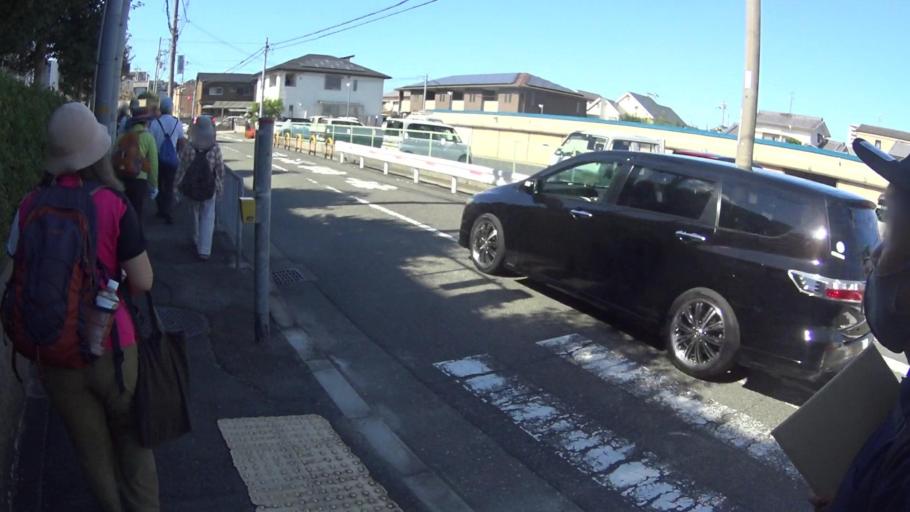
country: JP
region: Osaka
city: Izumi
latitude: 34.4950
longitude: 135.4212
